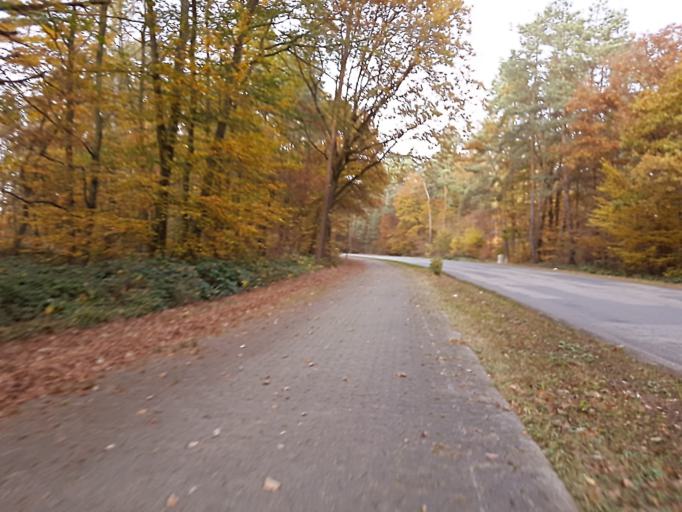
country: DE
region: Bavaria
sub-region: Regierungsbezirk Unterfranken
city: Worth am Main
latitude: 49.8128
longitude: 9.1464
